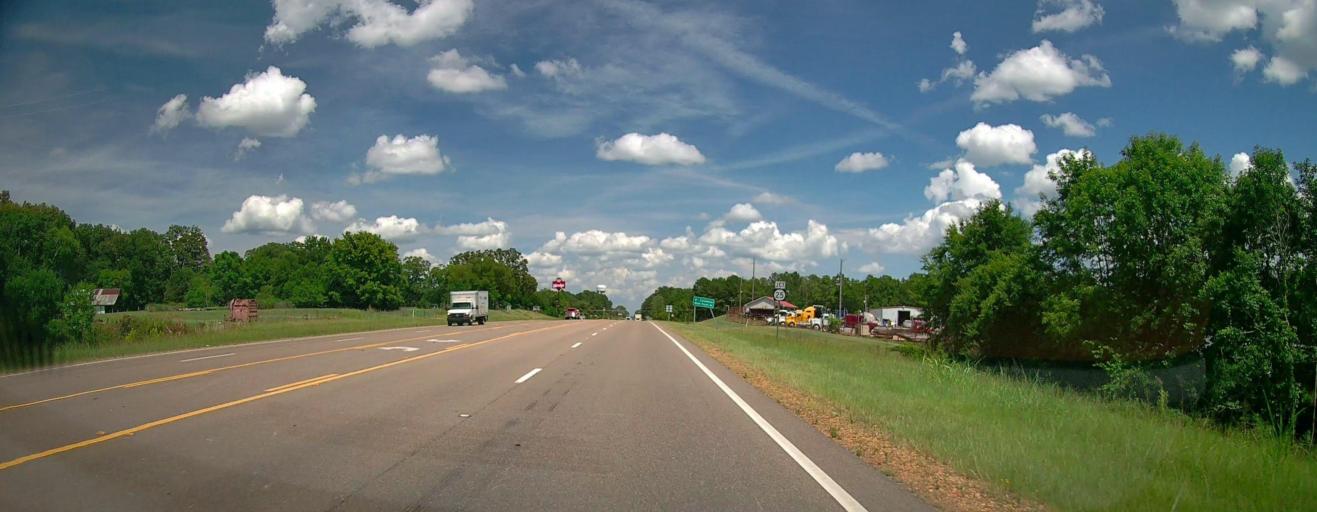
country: US
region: Mississippi
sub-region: Monroe County
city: Aberdeen
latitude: 33.8147
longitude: -88.5685
